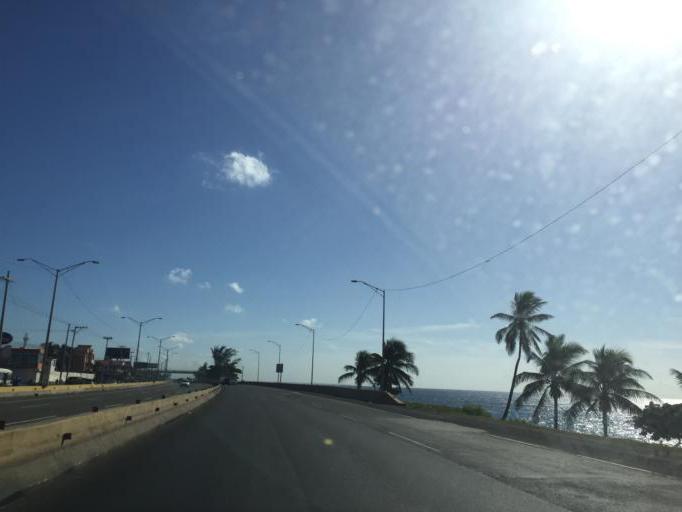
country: DO
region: Santo Domingo
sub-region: Santo Domingo
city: Santo Domingo Este
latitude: 18.4653
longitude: -69.8196
